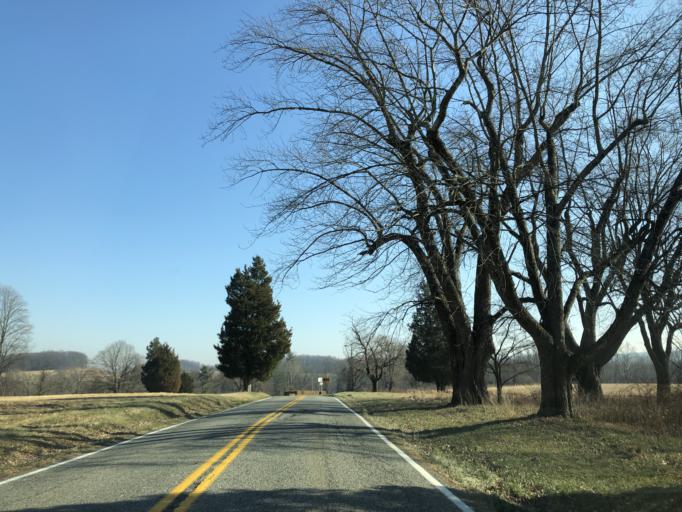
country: US
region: Pennsylvania
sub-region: Chester County
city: Chesterbrook
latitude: 40.0843
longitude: -75.4615
